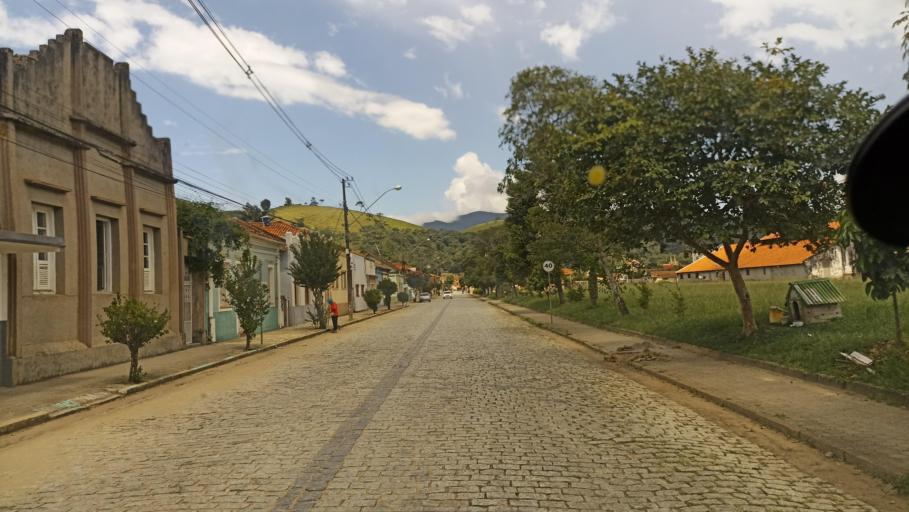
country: BR
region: Minas Gerais
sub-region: Passa Quatro
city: Passa Quatro
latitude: -22.3888
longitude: -44.9652
